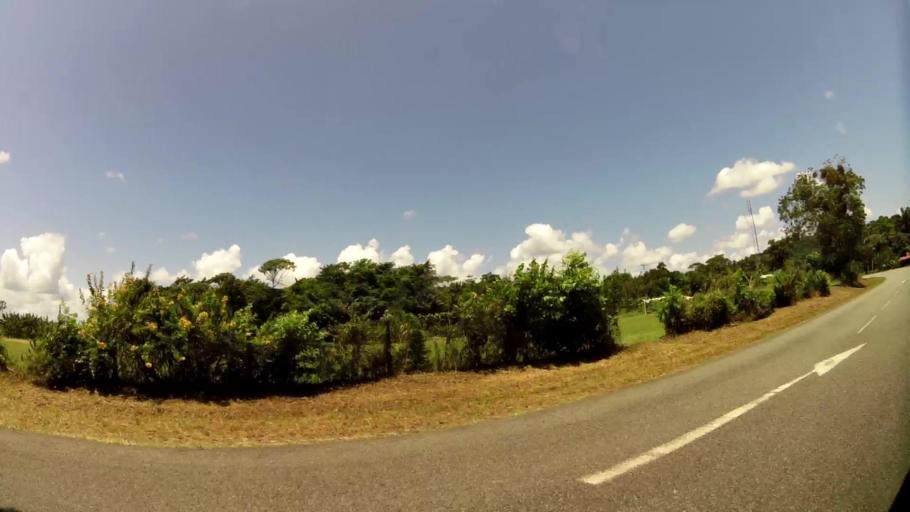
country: GF
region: Guyane
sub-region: Guyane
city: Cayenne
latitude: 4.8995
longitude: -52.3409
